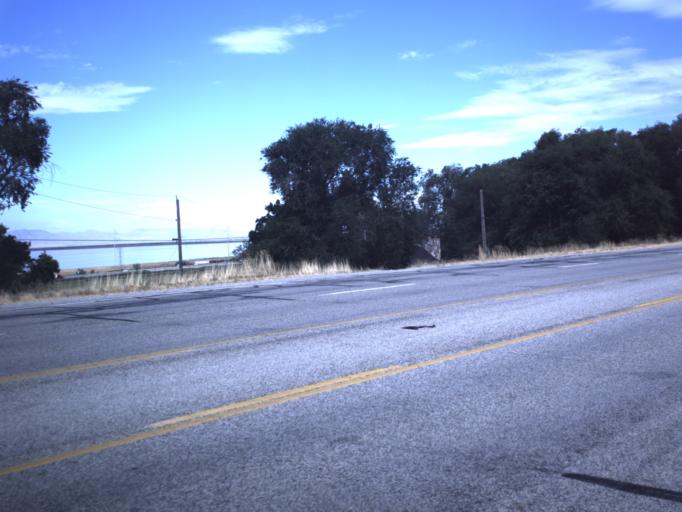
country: US
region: Utah
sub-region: Box Elder County
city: Willard
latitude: 41.3905
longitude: -112.0340
